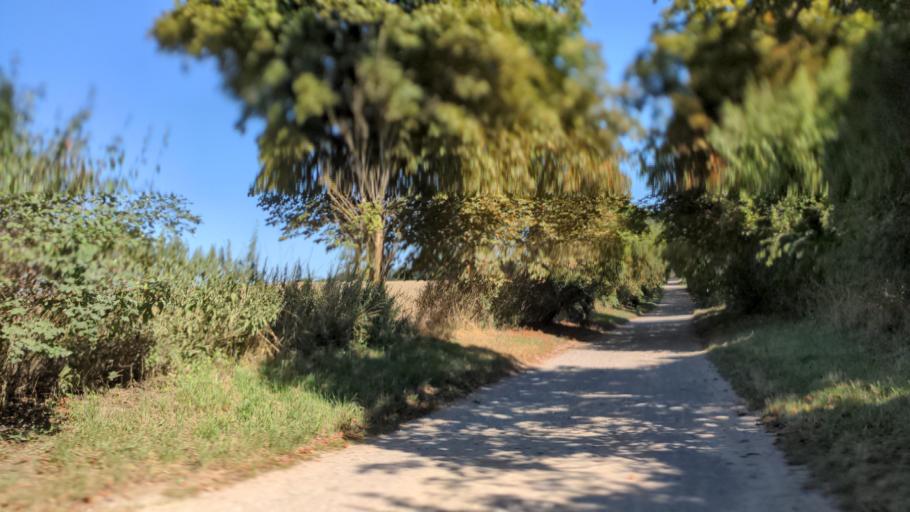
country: DE
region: Mecklenburg-Vorpommern
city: Klutz
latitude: 53.9773
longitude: 11.1702
